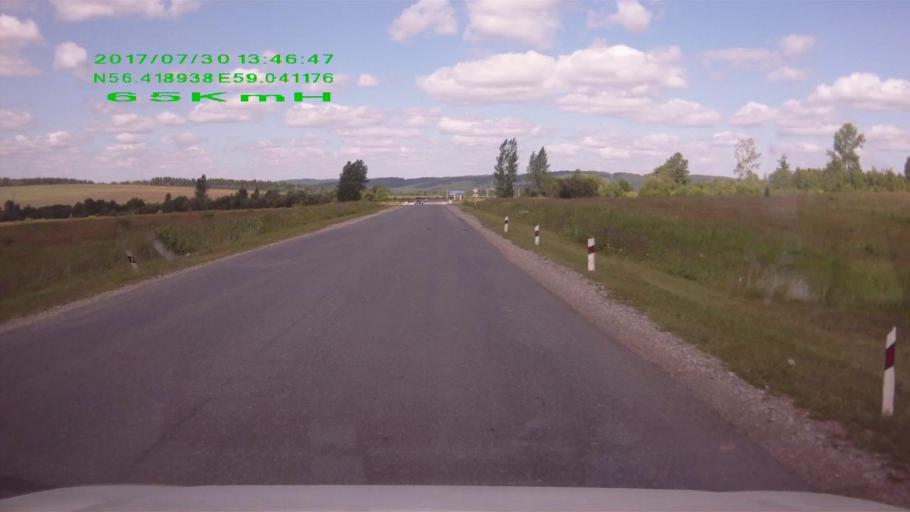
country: RU
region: Sverdlovsk
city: Mikhaylovsk
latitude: 56.4192
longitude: 59.0412
